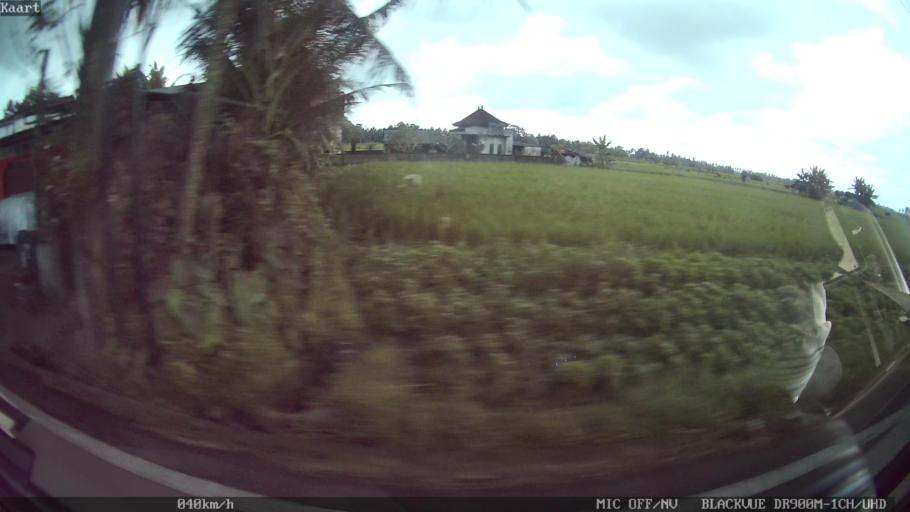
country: ID
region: Bali
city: Banjar Keraman
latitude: -8.5317
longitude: 115.2260
